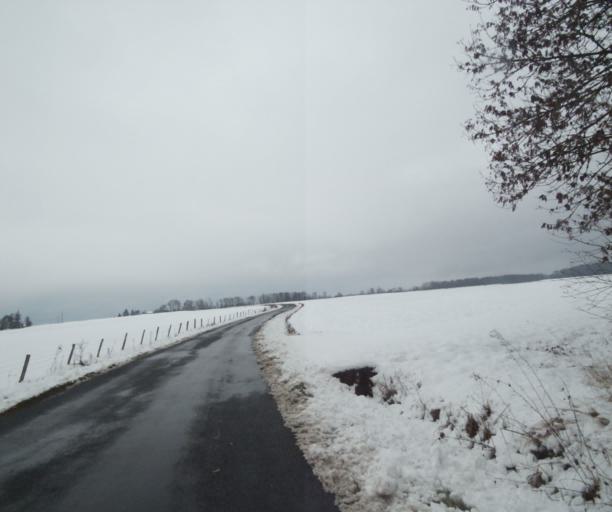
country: FR
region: Champagne-Ardenne
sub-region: Departement de la Haute-Marne
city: Laneuville-a-Remy
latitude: 48.4886
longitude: 4.8658
